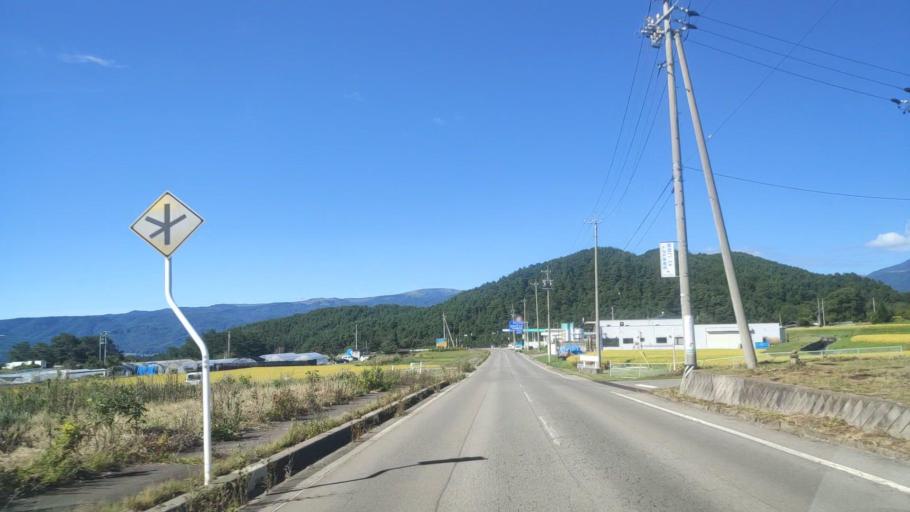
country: JP
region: Nagano
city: Chino
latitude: 35.9902
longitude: 138.2160
